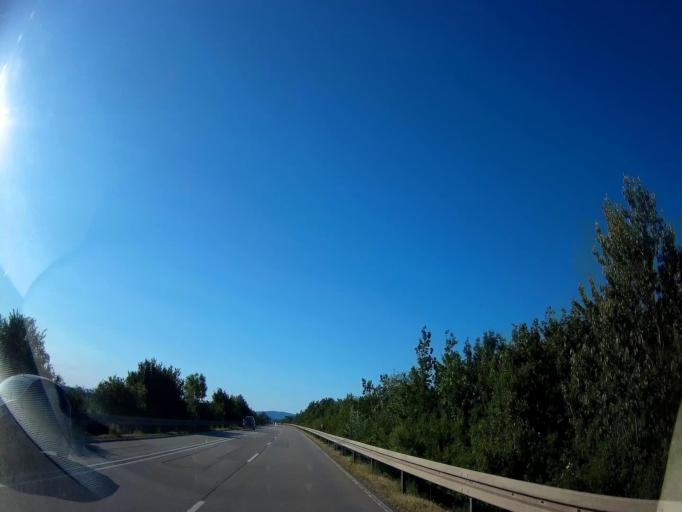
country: DE
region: Bavaria
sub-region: Lower Bavaria
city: Alterhofen
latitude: 48.8628
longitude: 12.6299
